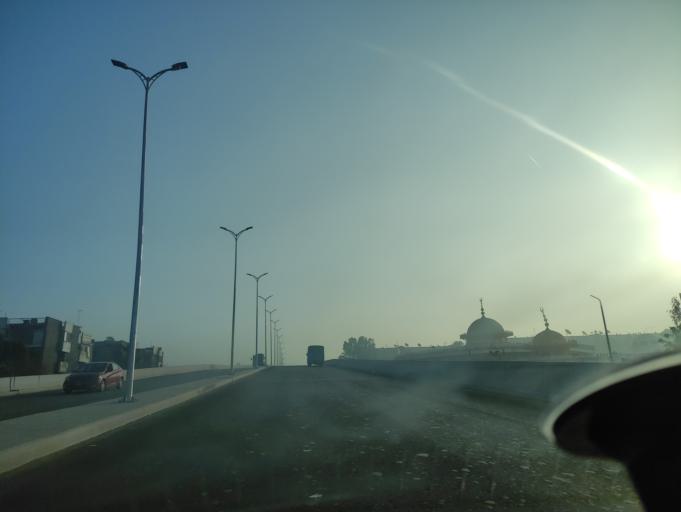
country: EG
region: Muhafazat al Qahirah
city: Cairo
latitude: 30.0464
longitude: 31.3547
